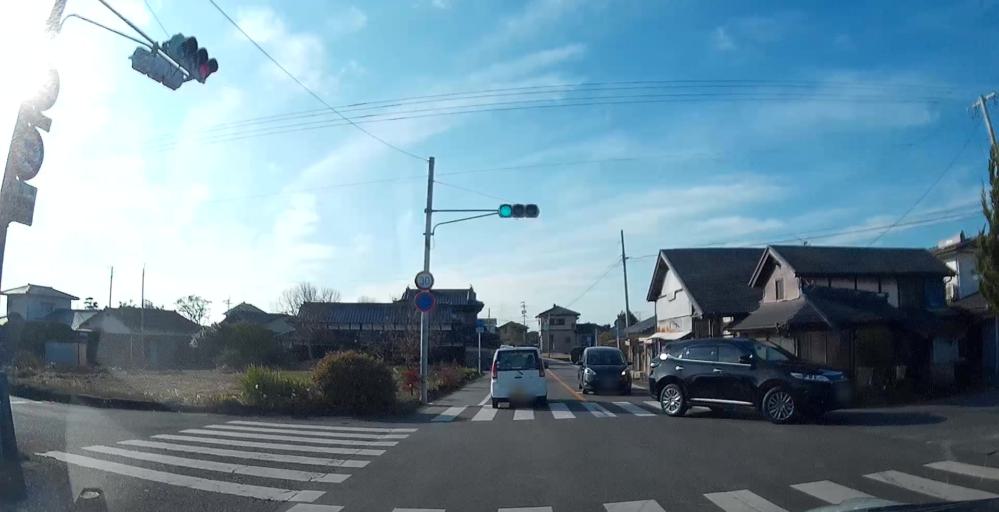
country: JP
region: Kumamoto
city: Uto
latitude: 32.7331
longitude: 130.6511
